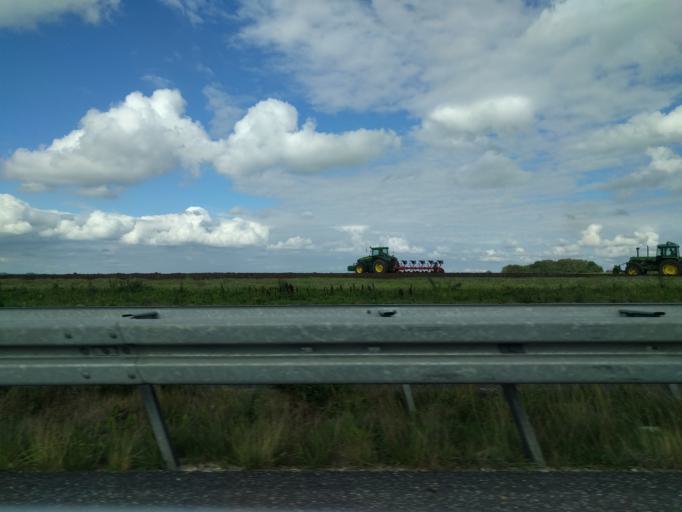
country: DK
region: Central Jutland
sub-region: Hedensted Kommune
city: Torring
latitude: 55.8314
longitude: 9.5142
